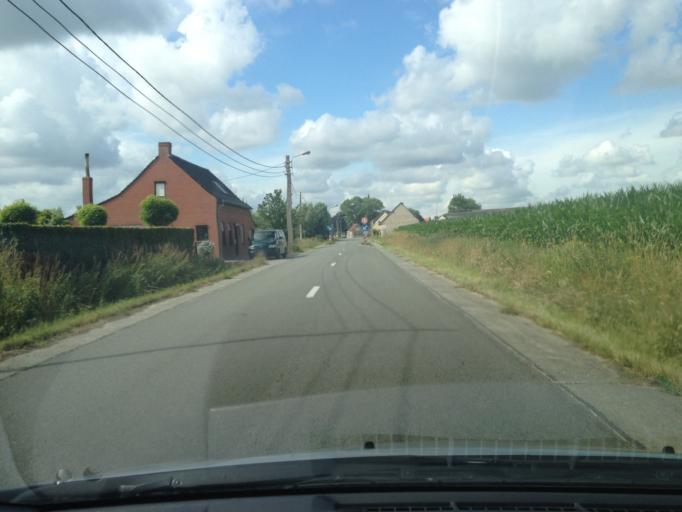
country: FR
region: Nord-Pas-de-Calais
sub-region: Departement du Nord
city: Killem
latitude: 50.9097
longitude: 2.6226
